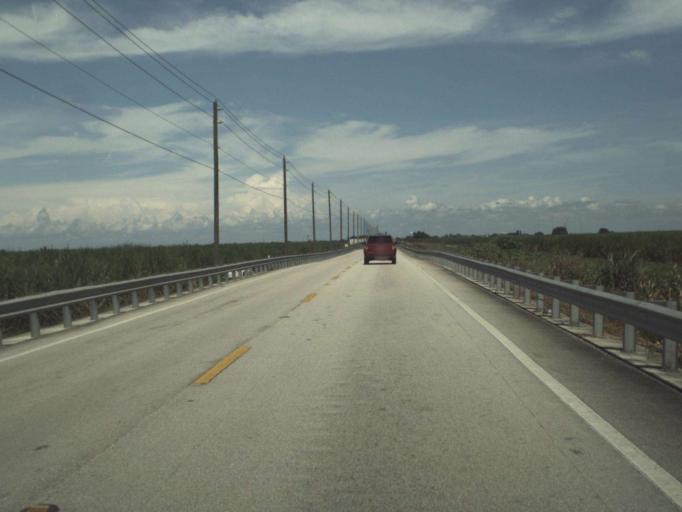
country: US
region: Florida
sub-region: Palm Beach County
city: Pahokee
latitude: 26.7761
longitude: -80.6533
